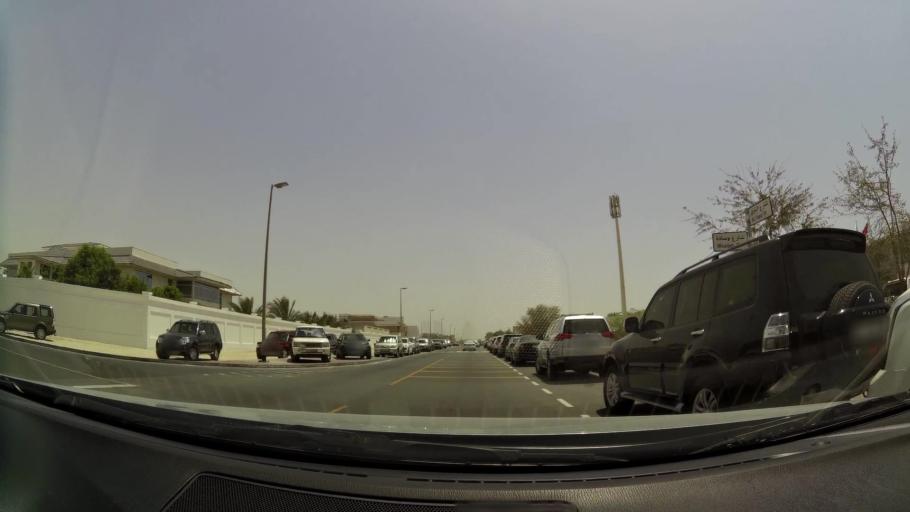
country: AE
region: Dubai
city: Dubai
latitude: 25.1351
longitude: 55.1964
